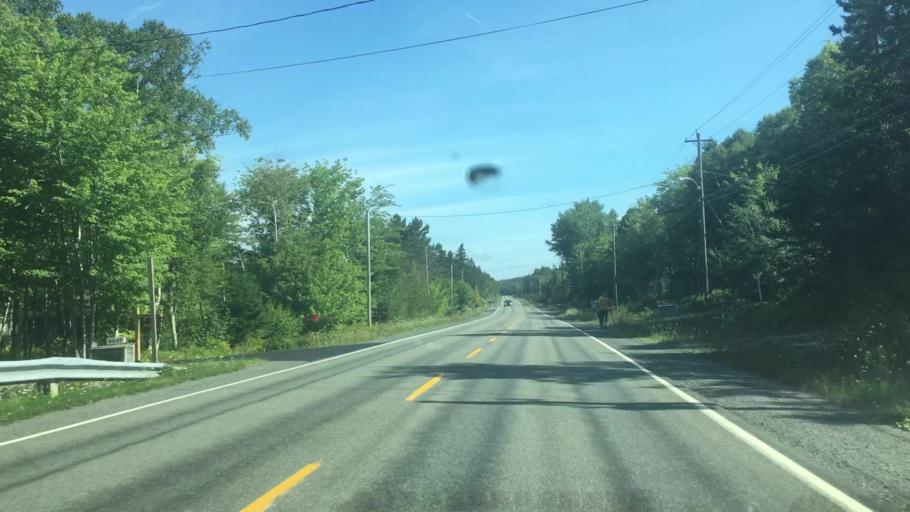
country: CA
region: Nova Scotia
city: Sydney
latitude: 45.9830
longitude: -60.4236
